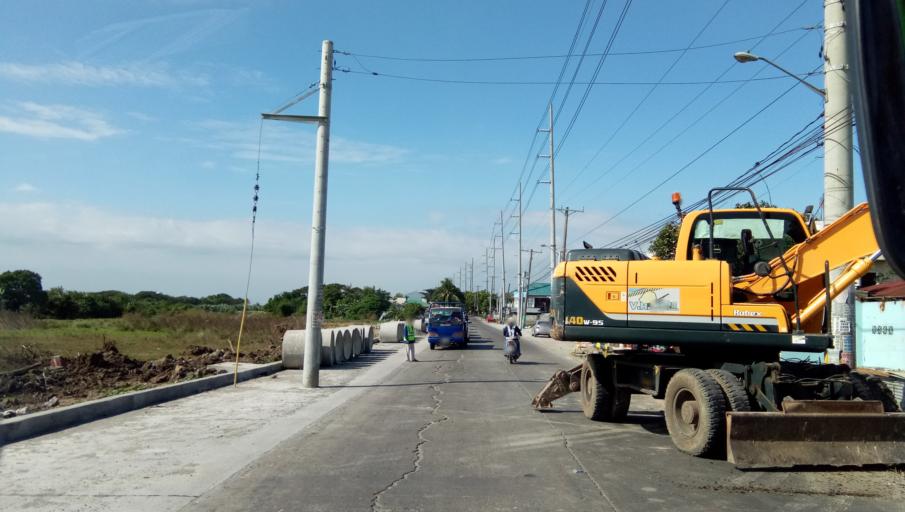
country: PH
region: Calabarzon
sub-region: Province of Cavite
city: Pasong Kawayan Primero
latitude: 14.3442
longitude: 120.9059
